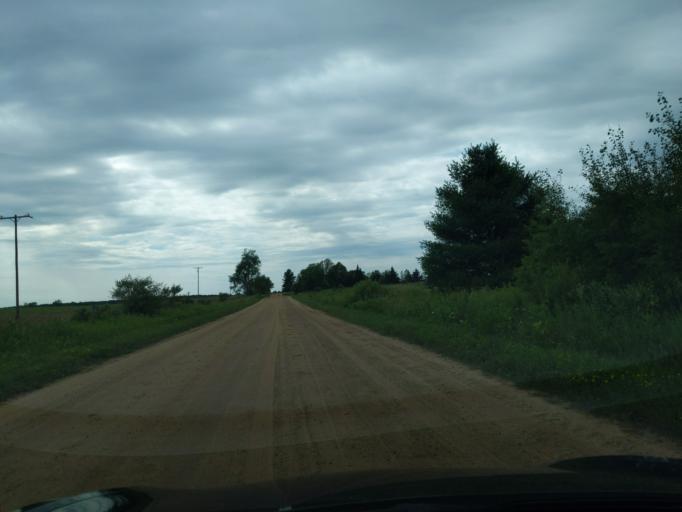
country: US
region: Michigan
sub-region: Clare County
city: Harrison
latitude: 44.0025
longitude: -84.9857
